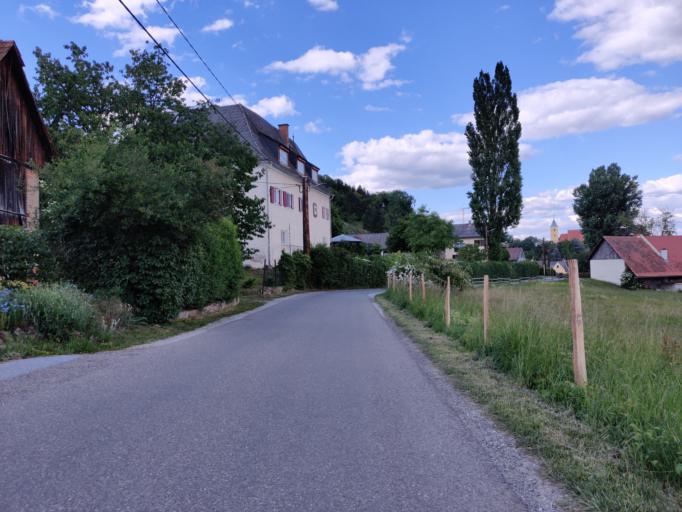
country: AT
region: Styria
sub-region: Graz Stadt
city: Wetzelsdorf
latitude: 47.0323
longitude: 15.3846
